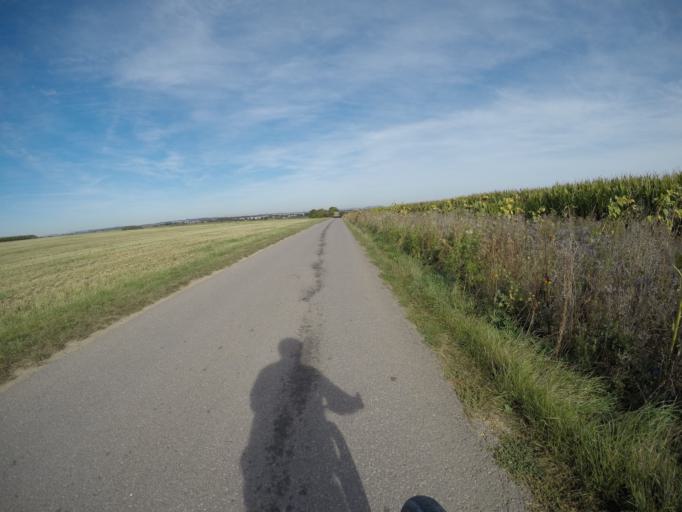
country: DE
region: Baden-Wuerttemberg
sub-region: Regierungsbezirk Stuttgart
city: Korntal
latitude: 48.8394
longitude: 9.1136
